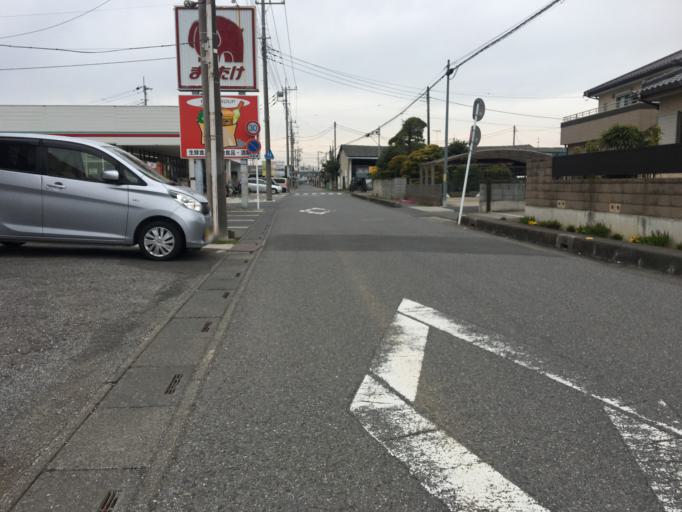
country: JP
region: Saitama
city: Kisai
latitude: 36.1017
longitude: 139.5772
